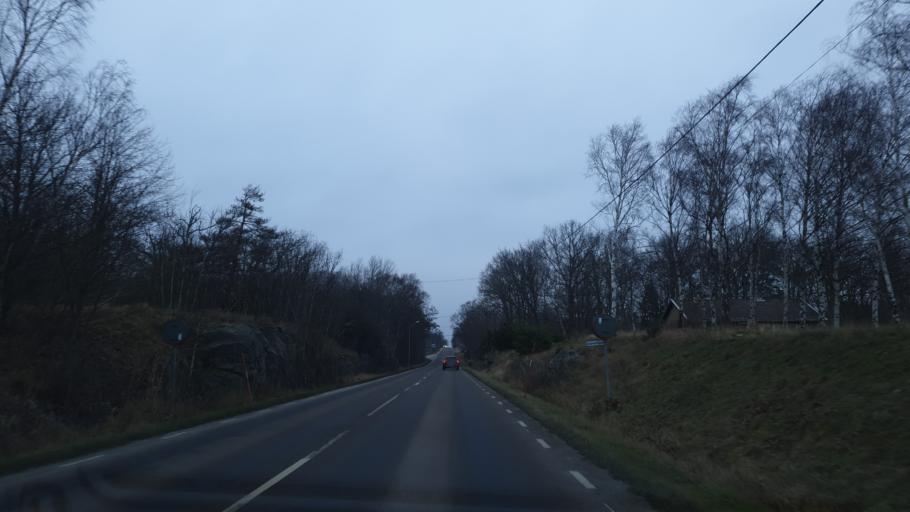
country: SE
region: Blekinge
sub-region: Karlskrona Kommun
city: Sturko
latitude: 56.1211
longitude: 15.7349
